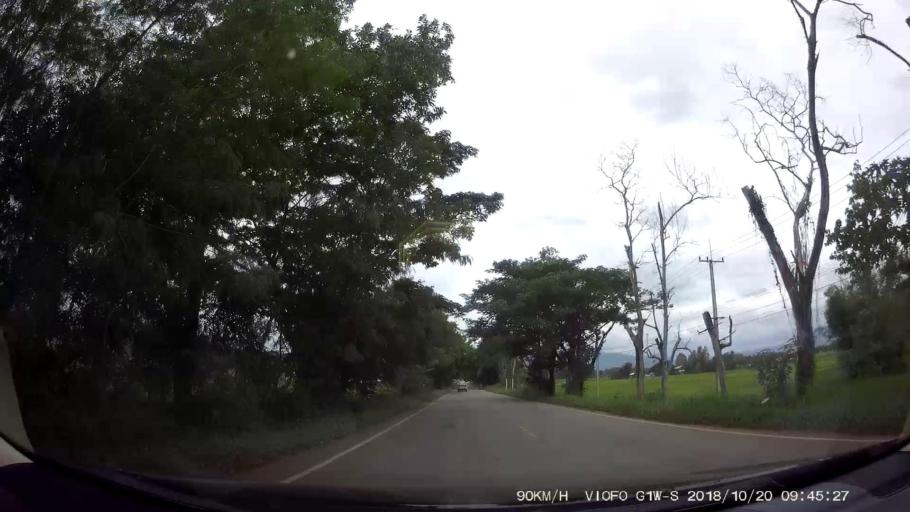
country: TH
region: Chaiyaphum
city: Khon San
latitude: 16.4907
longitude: 101.9359
